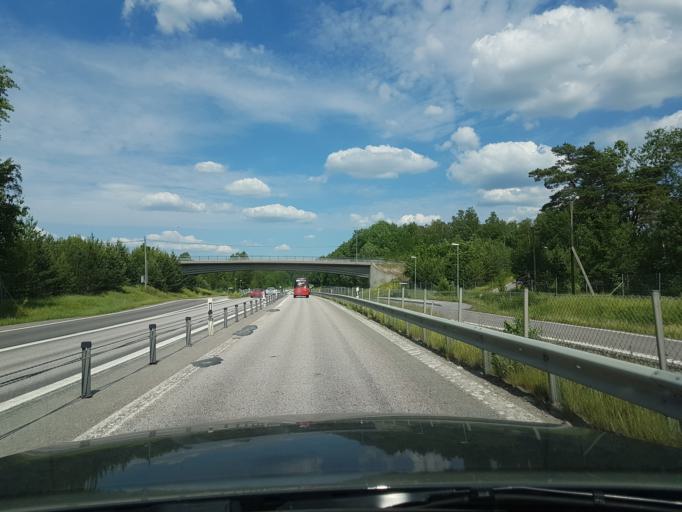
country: SE
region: Stockholm
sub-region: Vallentuna Kommun
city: Vallentuna
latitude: 59.5100
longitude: 18.1755
